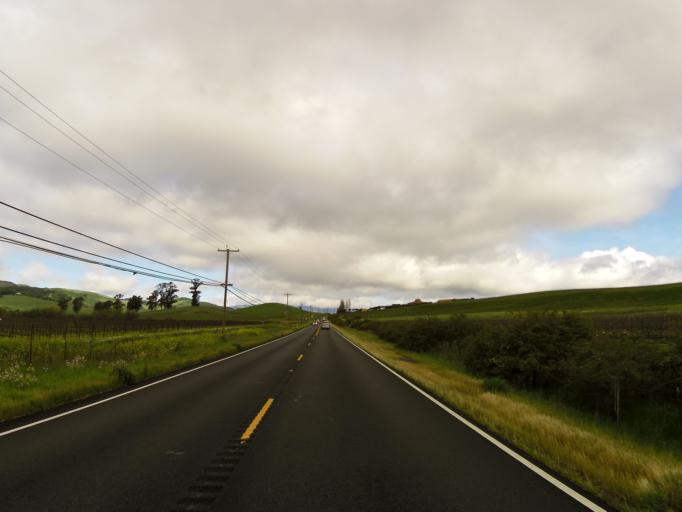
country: US
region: California
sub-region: Sonoma County
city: Temelec
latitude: 38.2025
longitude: -122.4489
